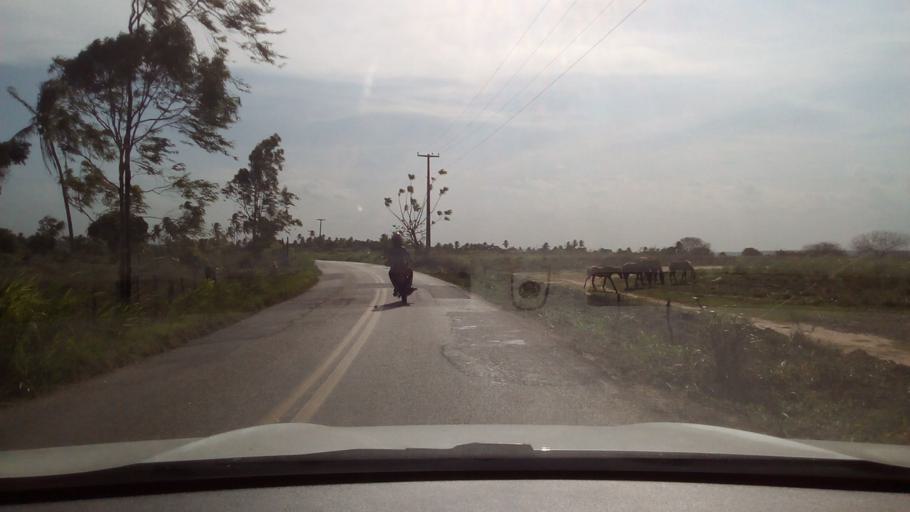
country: BR
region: Rio Grande do Norte
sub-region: Ares
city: Ares
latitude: -6.2379
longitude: -35.1745
